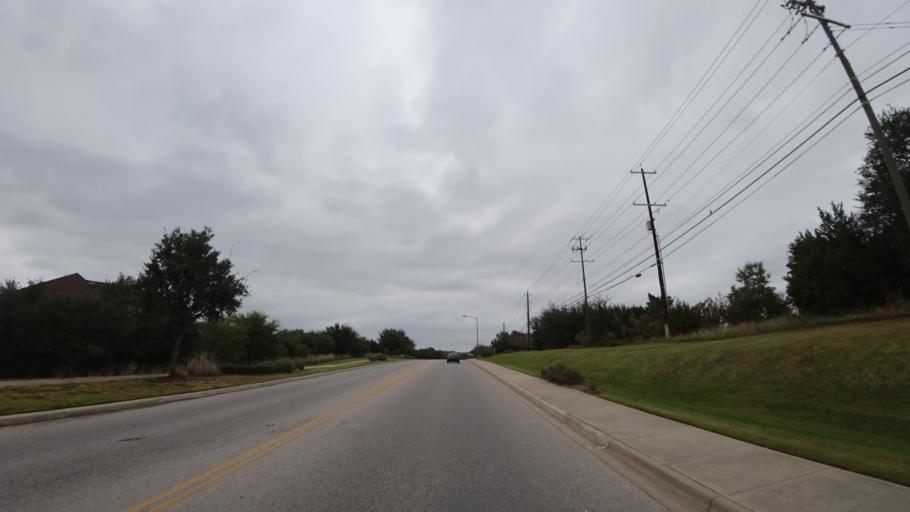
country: US
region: Texas
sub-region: Travis County
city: Bee Cave
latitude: 30.3516
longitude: -97.9117
